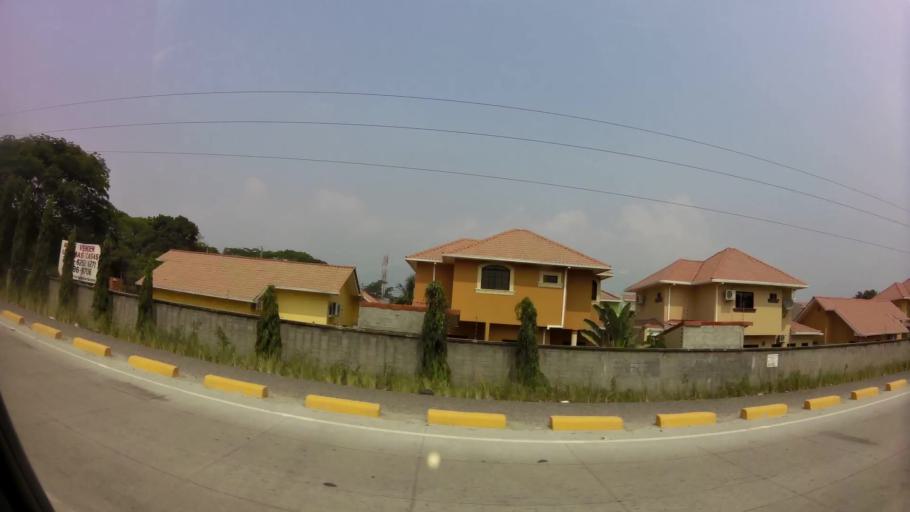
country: HN
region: Cortes
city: San Pedro Sula
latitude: 15.5471
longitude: -87.9981
